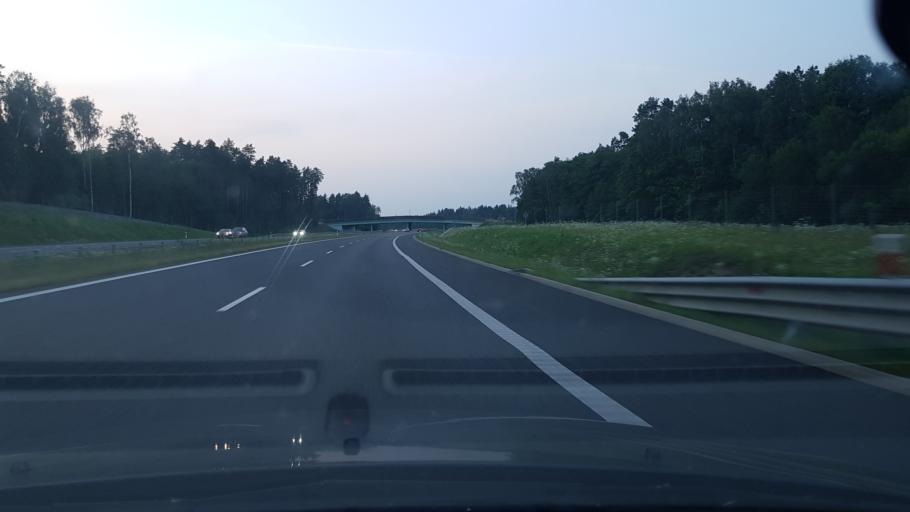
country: PL
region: Warmian-Masurian Voivodeship
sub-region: Powiat olsztynski
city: Olsztynek
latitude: 53.4566
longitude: 20.3215
